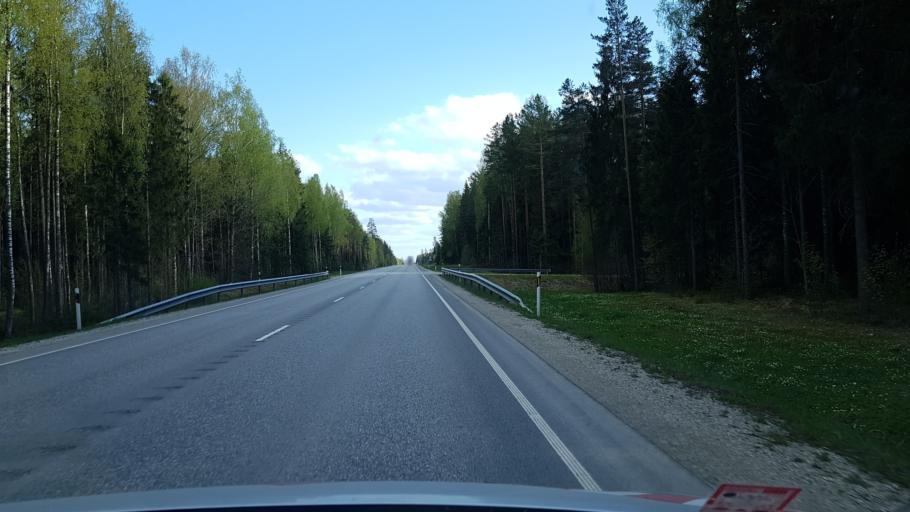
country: EE
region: Vorumaa
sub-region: Voru linn
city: Voru
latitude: 57.9539
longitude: 26.7936
